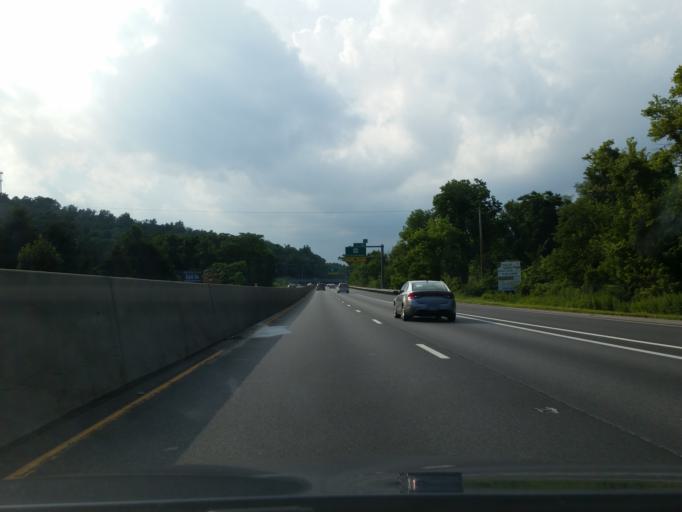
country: US
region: Pennsylvania
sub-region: York County
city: Valley Green
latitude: 40.1423
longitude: -76.8105
